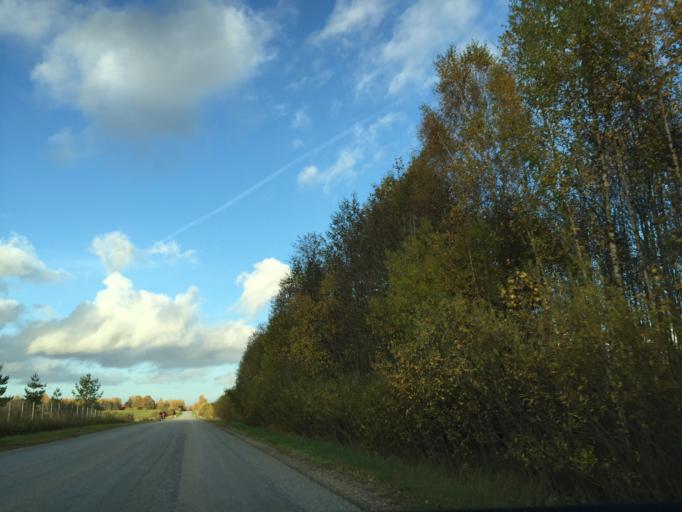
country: LV
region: Ogre
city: Jumprava
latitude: 56.7858
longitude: 25.0244
